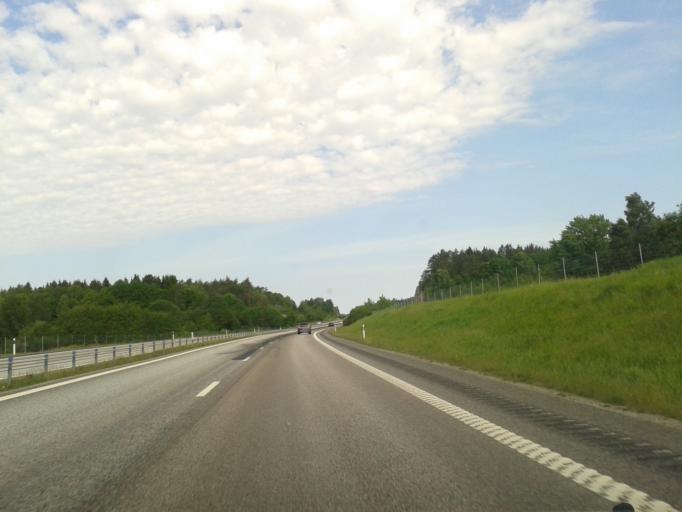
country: SE
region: Vaestra Goetaland
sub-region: Munkedals Kommun
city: Munkedal
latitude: 58.5435
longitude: 11.5204
